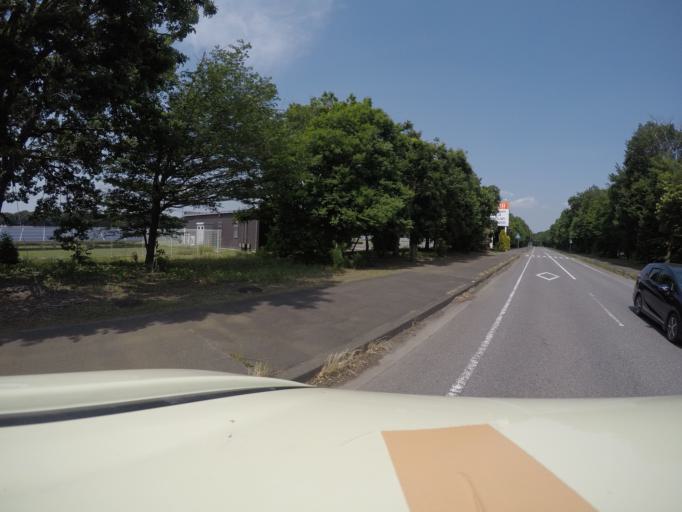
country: JP
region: Ibaraki
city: Iwai
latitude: 36.0556
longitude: 139.9193
